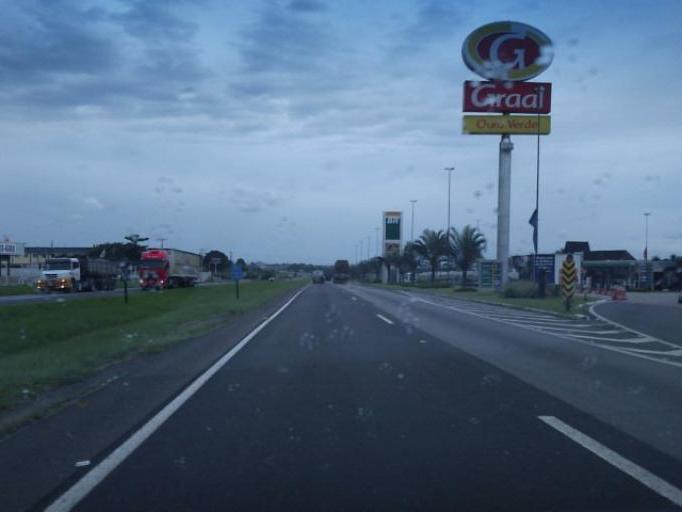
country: BR
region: Sao Paulo
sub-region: Registro
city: Registro
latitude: -24.4752
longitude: -47.8270
